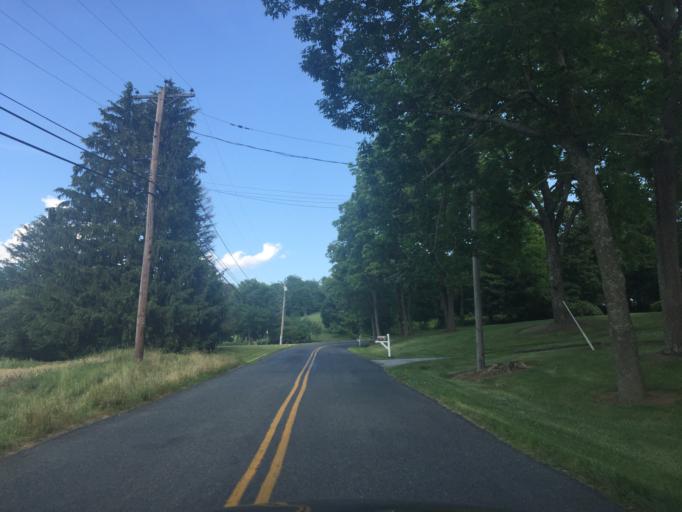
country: US
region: Maryland
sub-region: Harford County
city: Jarrettsville
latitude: 39.6578
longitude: -76.4814
